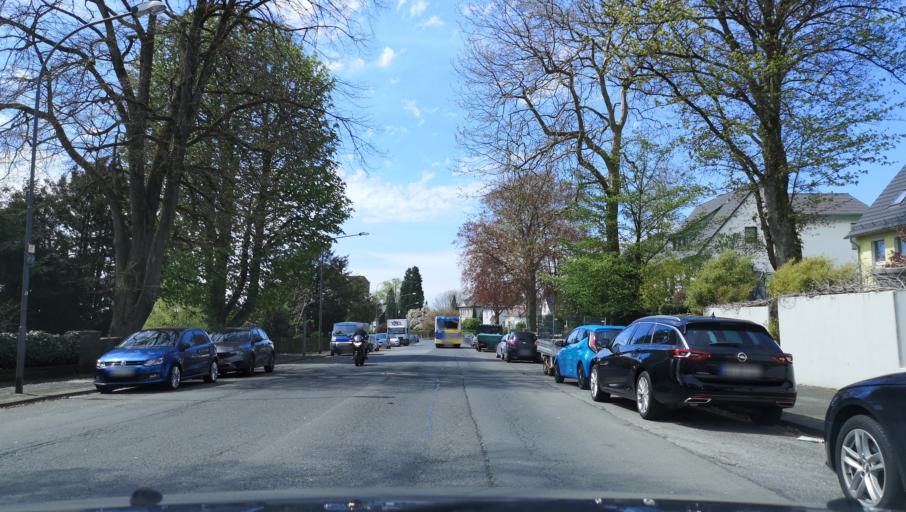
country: DE
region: North Rhine-Westphalia
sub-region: Regierungsbezirk Dusseldorf
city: Remscheid
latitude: 51.1662
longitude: 7.1968
